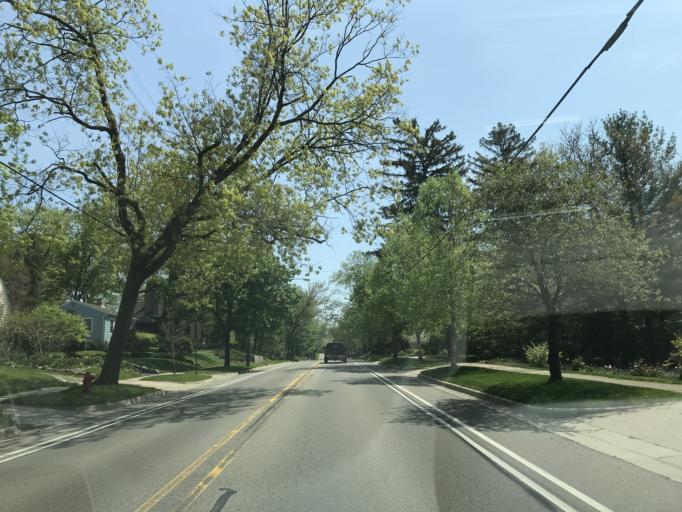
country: US
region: Michigan
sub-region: Washtenaw County
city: Ann Arbor
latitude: 42.2718
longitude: -83.7584
